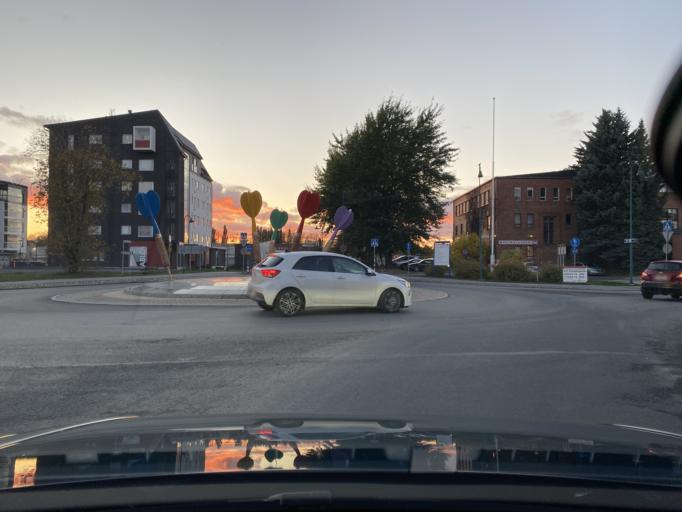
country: FI
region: Pirkanmaa
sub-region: Tampere
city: Lempaeaelae
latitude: 61.3150
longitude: 23.7584
